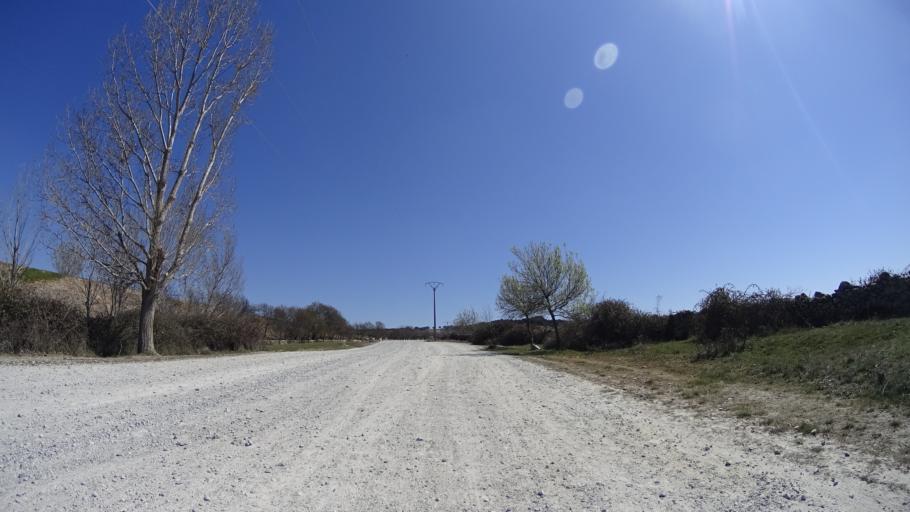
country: ES
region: Madrid
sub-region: Provincia de Madrid
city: Colmenar Viejo
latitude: 40.7048
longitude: -3.7774
